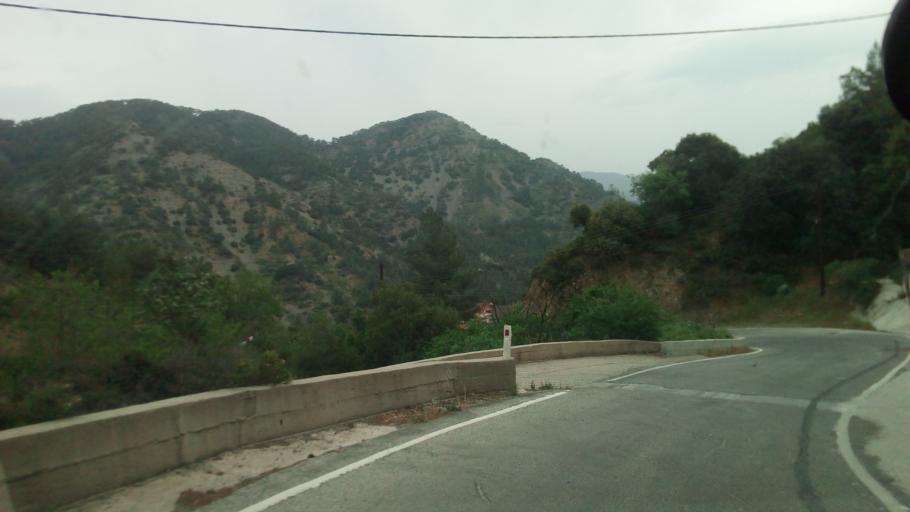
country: CY
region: Lefkosia
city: Kakopetria
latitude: 34.9631
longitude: 32.7474
